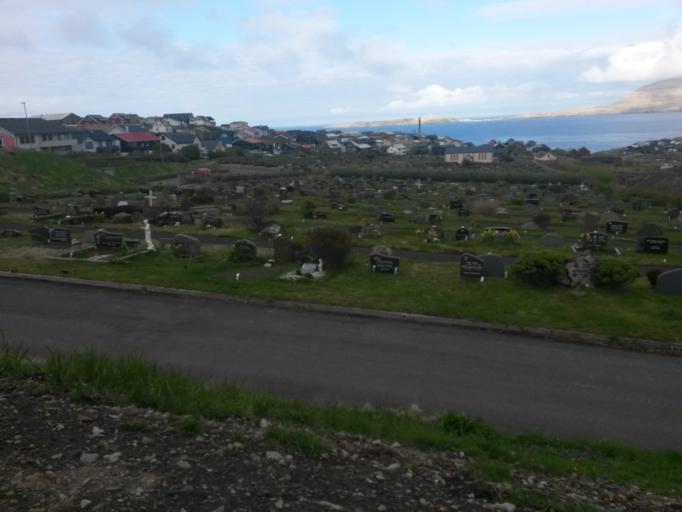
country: FO
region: Streymoy
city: Argir
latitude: 62.0001
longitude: -6.7958
